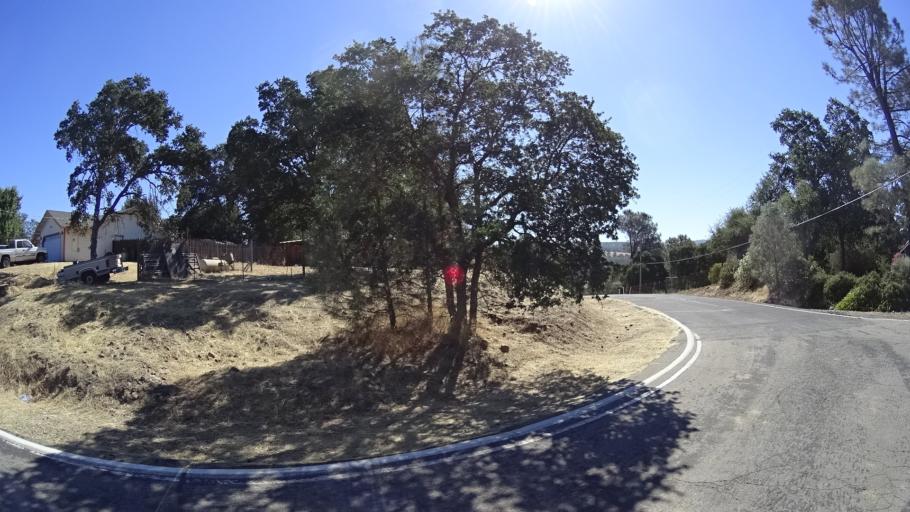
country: US
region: California
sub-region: Calaveras County
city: Rancho Calaveras
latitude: 38.0912
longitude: -120.8609
